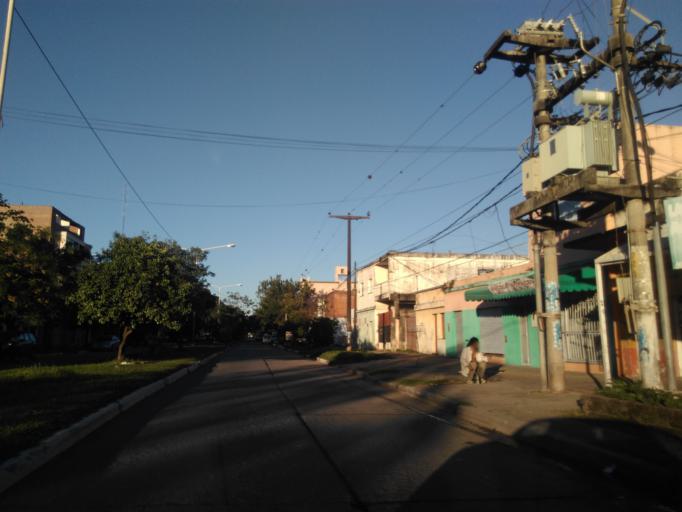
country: AR
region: Chaco
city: Resistencia
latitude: -27.4550
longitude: -58.9997
